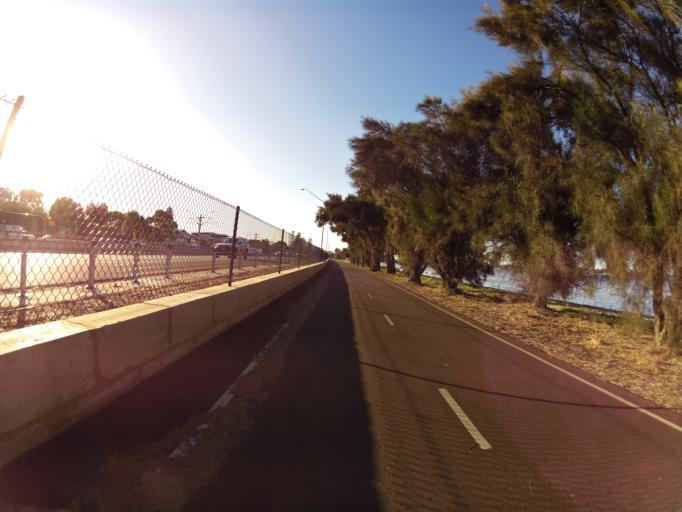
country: AU
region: Western Australia
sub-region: South Perth
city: Como
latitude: -31.9876
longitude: 115.8527
